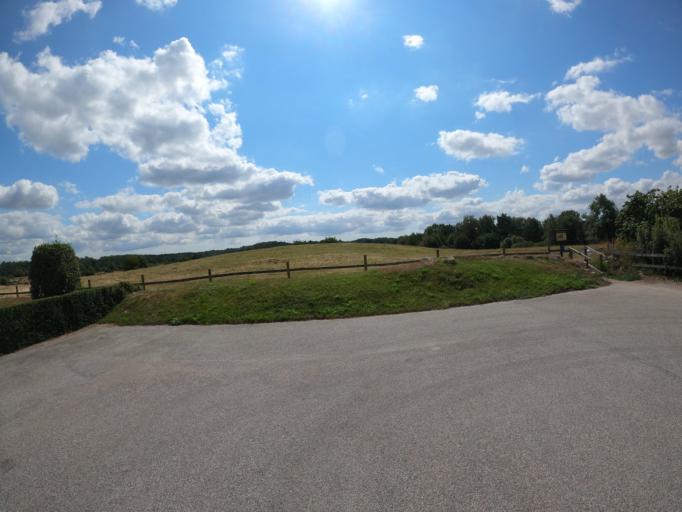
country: SE
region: Skane
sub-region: Lunds Kommun
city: Genarp
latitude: 55.5933
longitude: 13.4009
